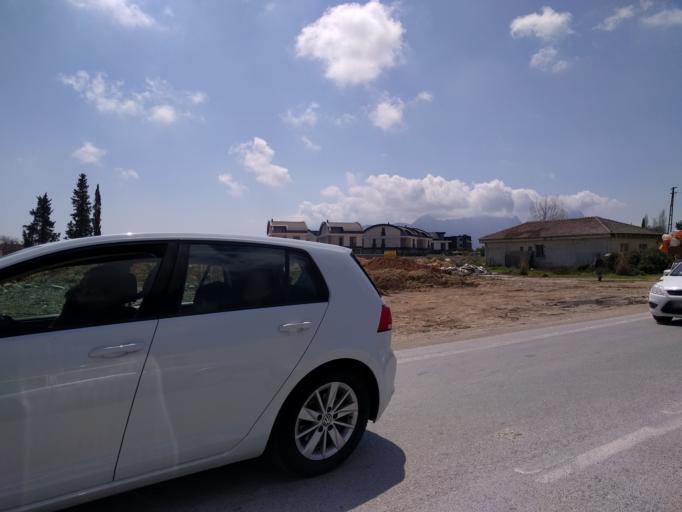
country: TR
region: Antalya
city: Cakirlar
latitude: 36.8970
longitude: 30.6090
